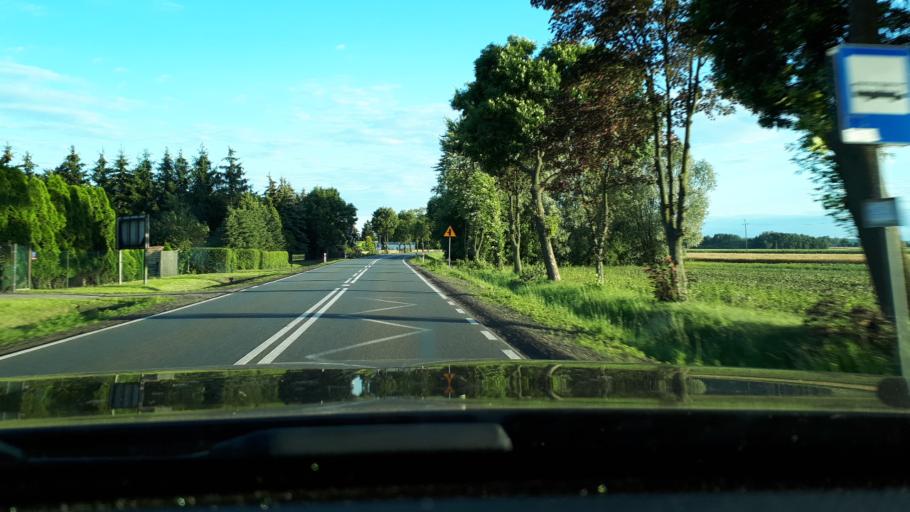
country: PL
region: Masovian Voivodeship
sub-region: Powiat ciechanowski
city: Ciechanow
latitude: 52.8299
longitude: 20.6186
